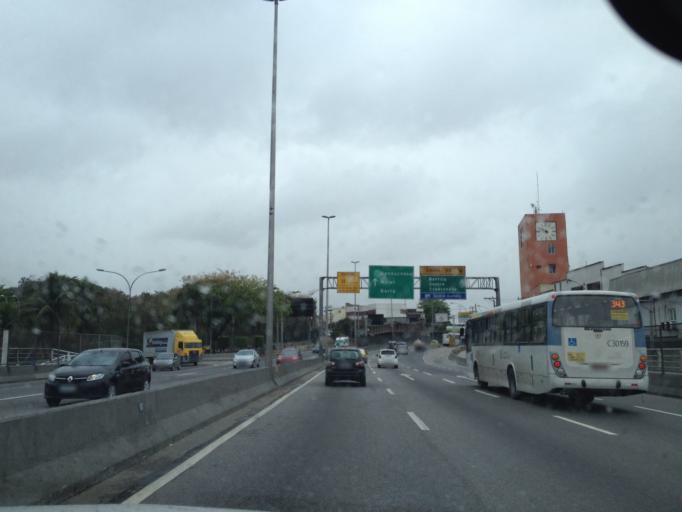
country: BR
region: Rio de Janeiro
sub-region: Rio De Janeiro
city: Rio de Janeiro
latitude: -22.8711
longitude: -43.2464
